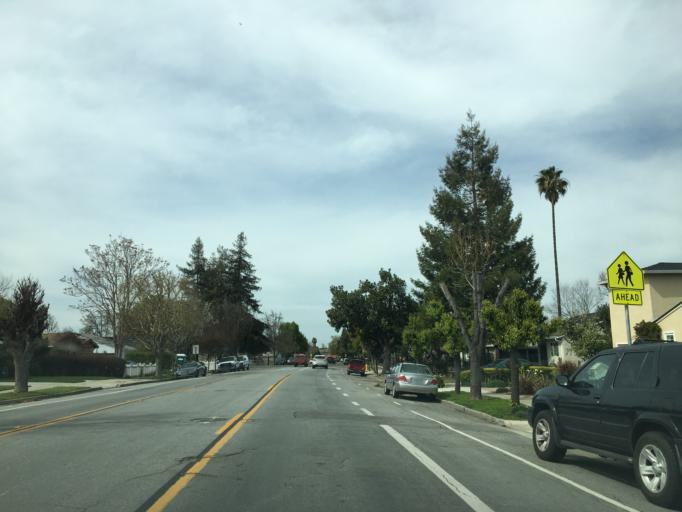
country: US
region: California
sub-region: Santa Clara County
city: Buena Vista
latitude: 37.3009
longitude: -121.8850
